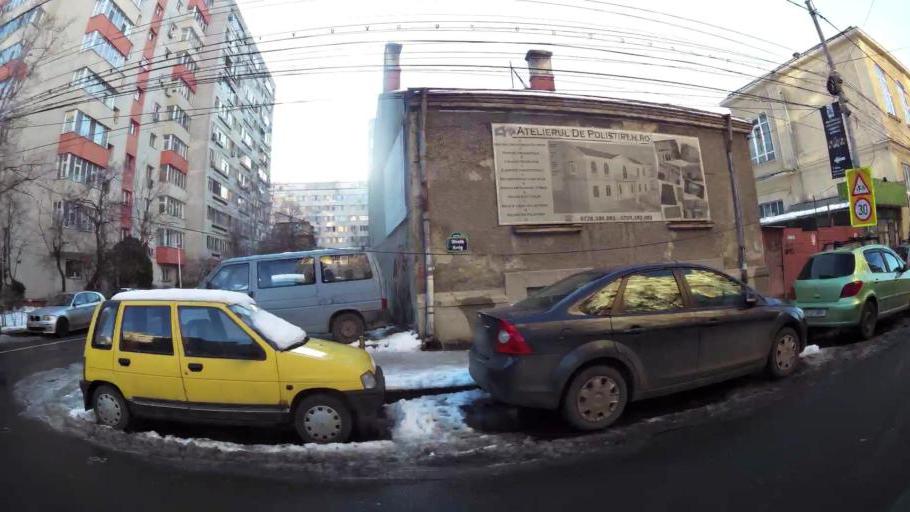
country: RO
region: Bucuresti
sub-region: Municipiul Bucuresti
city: Bucharest
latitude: 44.4439
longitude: 26.1320
